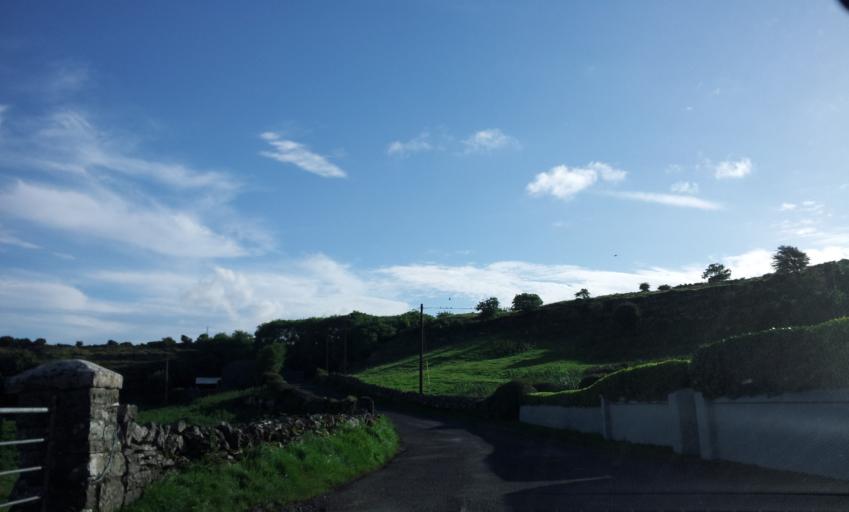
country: IE
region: Connaught
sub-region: County Galway
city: Bearna
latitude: 53.0340
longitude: -9.1358
